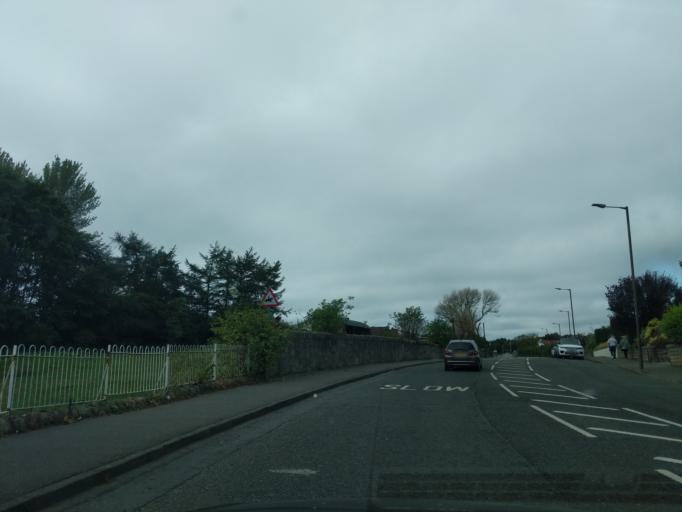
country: GB
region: Scotland
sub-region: Midlothian
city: Loanhead
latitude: 55.9125
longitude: -3.1725
